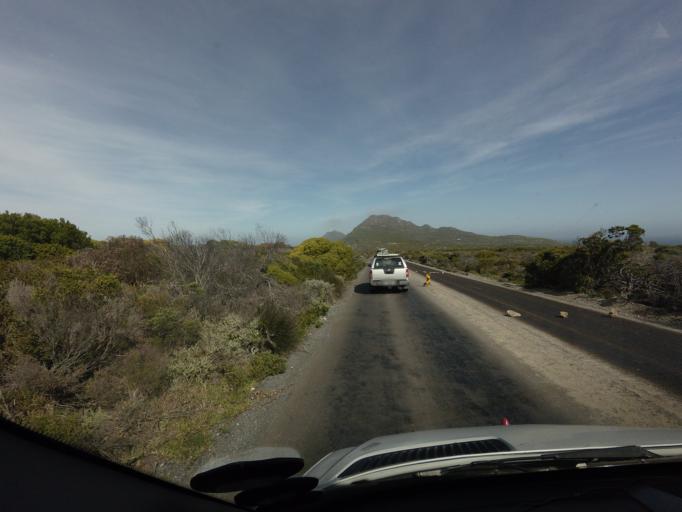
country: ZA
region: Western Cape
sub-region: City of Cape Town
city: Retreat
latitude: -34.3310
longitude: 18.4608
